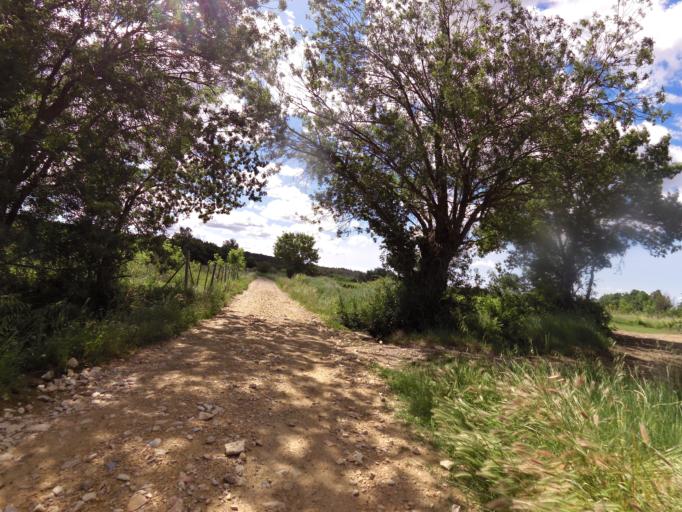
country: FR
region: Languedoc-Roussillon
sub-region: Departement du Gard
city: Calvisson
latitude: 43.7671
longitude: 4.2112
